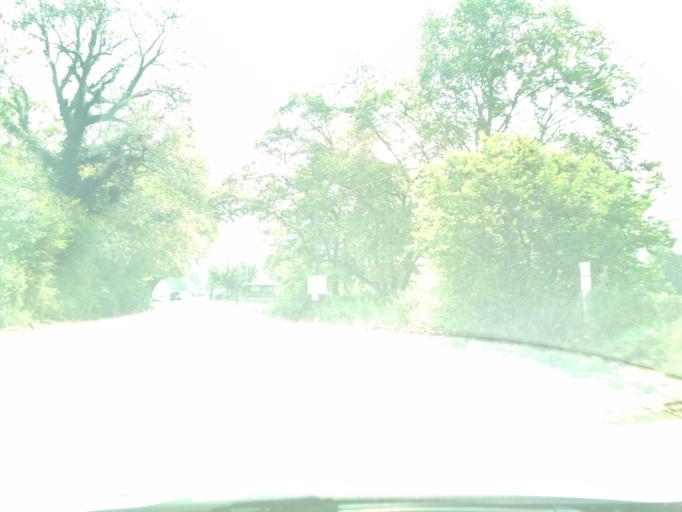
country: GR
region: Central Greece
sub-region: Nomos Evvoias
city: Prokopion
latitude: 38.7216
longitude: 23.5112
